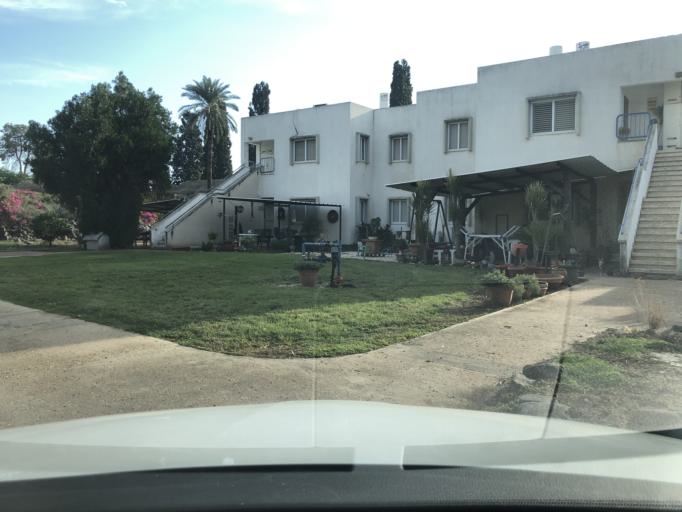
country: IL
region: Northern District
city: Yavne'el
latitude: 32.6611
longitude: 35.5814
